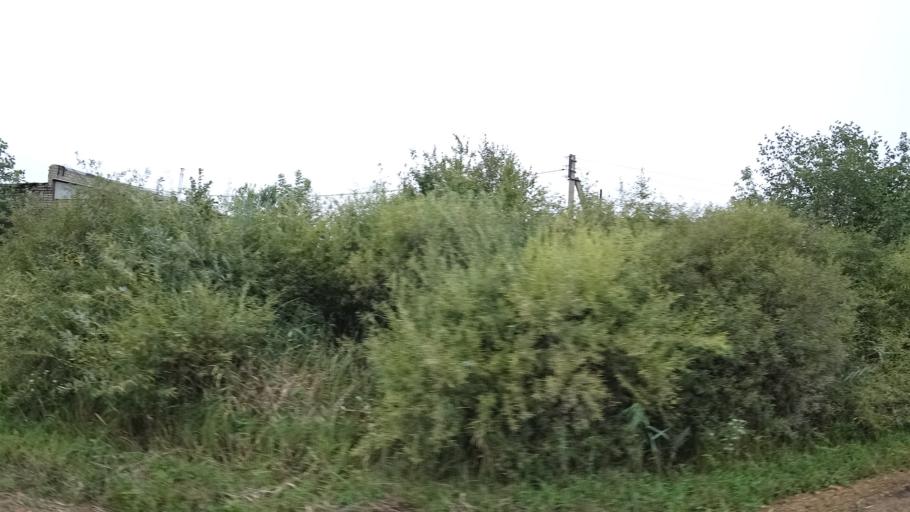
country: RU
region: Primorskiy
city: Chernigovka
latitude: 44.3343
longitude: 132.5232
